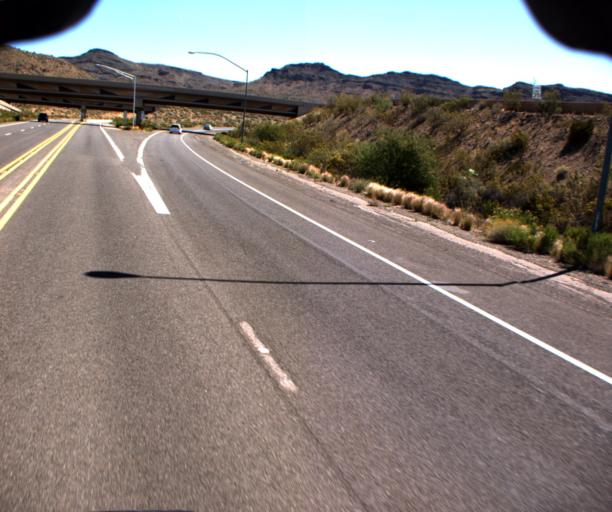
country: US
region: Arizona
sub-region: Mohave County
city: Kingman
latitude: 35.2205
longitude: -114.1284
